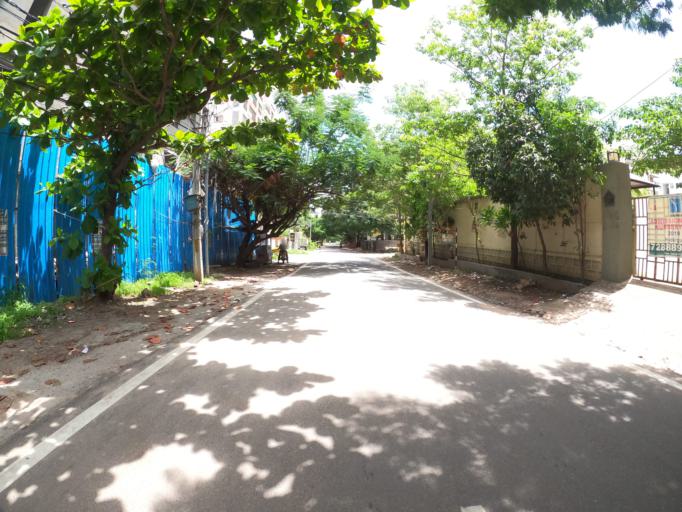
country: IN
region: Telangana
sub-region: Hyderabad
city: Hyderabad
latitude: 17.3697
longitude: 78.4227
